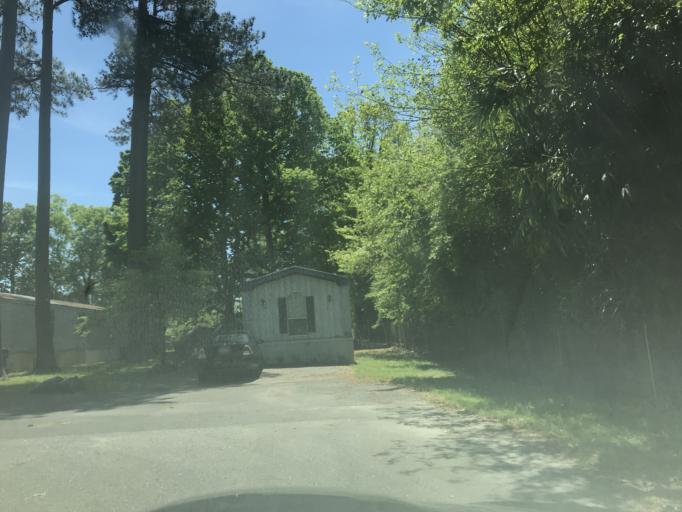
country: US
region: North Carolina
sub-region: Wake County
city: Raleigh
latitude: 35.8253
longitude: -78.5774
